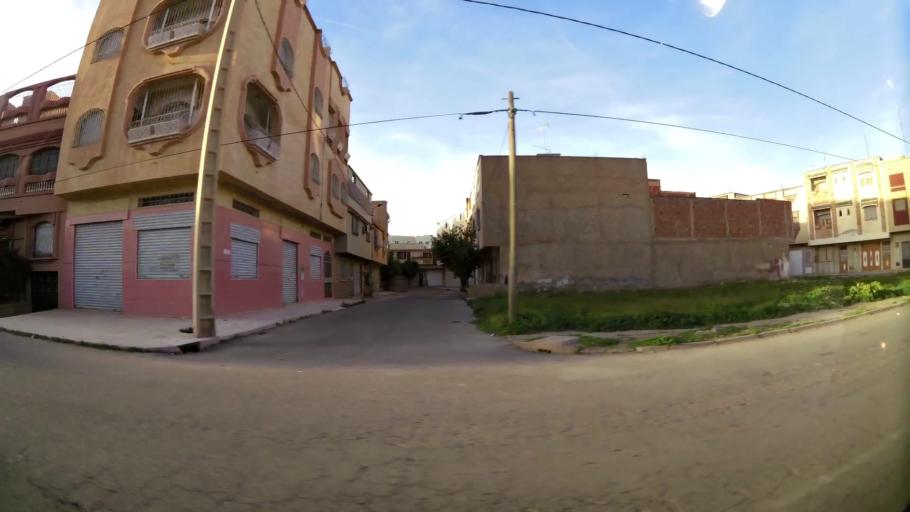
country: MA
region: Oriental
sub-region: Oujda-Angad
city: Oujda
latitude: 34.6773
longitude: -1.8950
